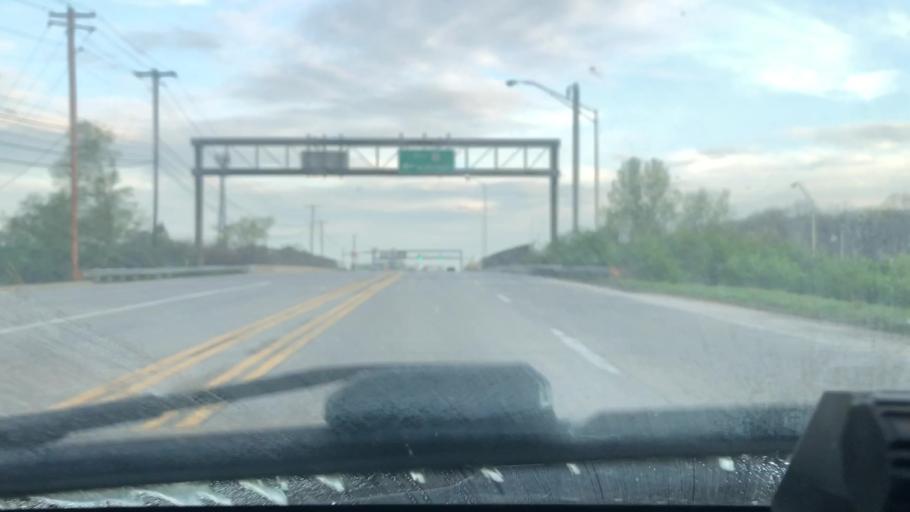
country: US
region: Pennsylvania
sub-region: Northampton County
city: Bethlehem
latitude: 40.6493
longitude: -75.4100
